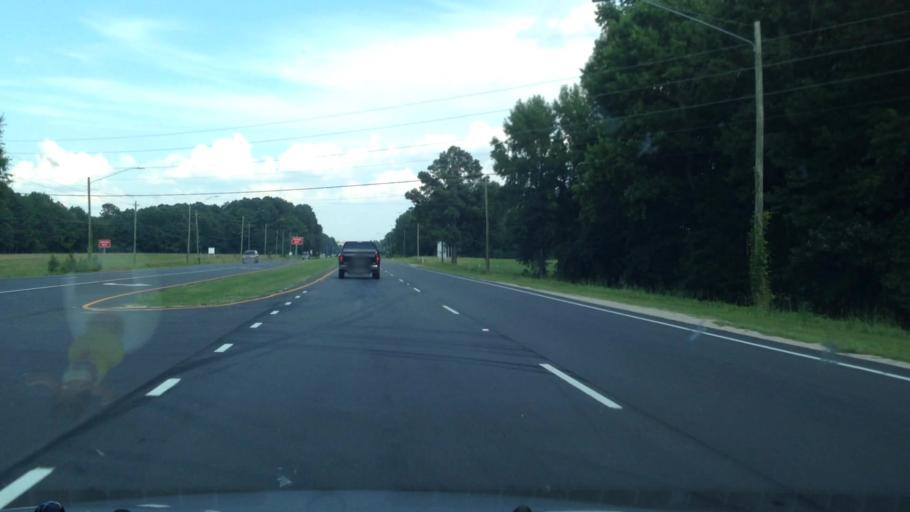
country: US
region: North Carolina
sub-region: Harnett County
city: Lillington
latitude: 35.4100
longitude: -78.7800
